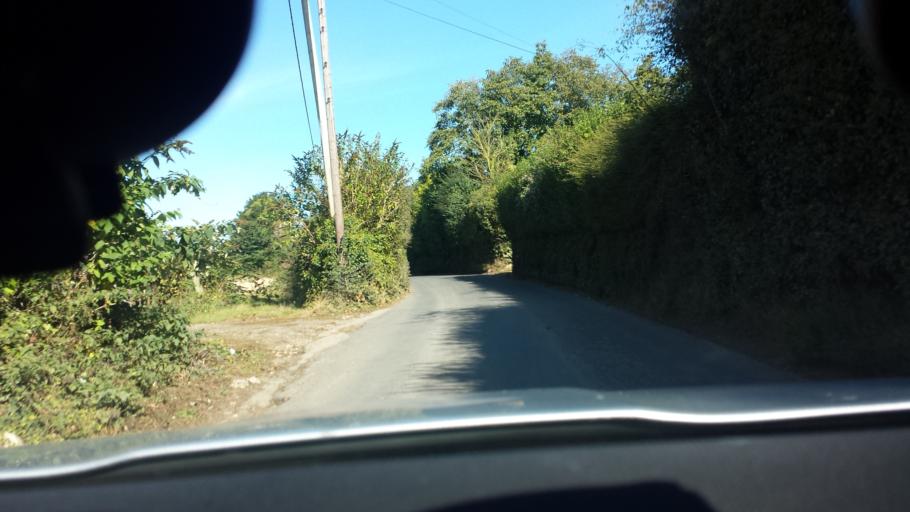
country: GB
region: England
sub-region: Kent
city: Staplehurst
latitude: 51.2177
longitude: 0.5709
